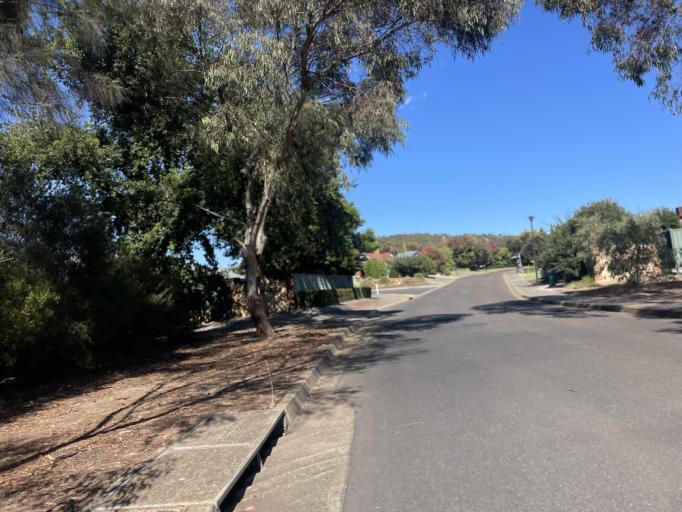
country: AU
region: South Australia
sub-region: Clare and Gilbert Valleys
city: Clare
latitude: -33.8443
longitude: 138.6128
